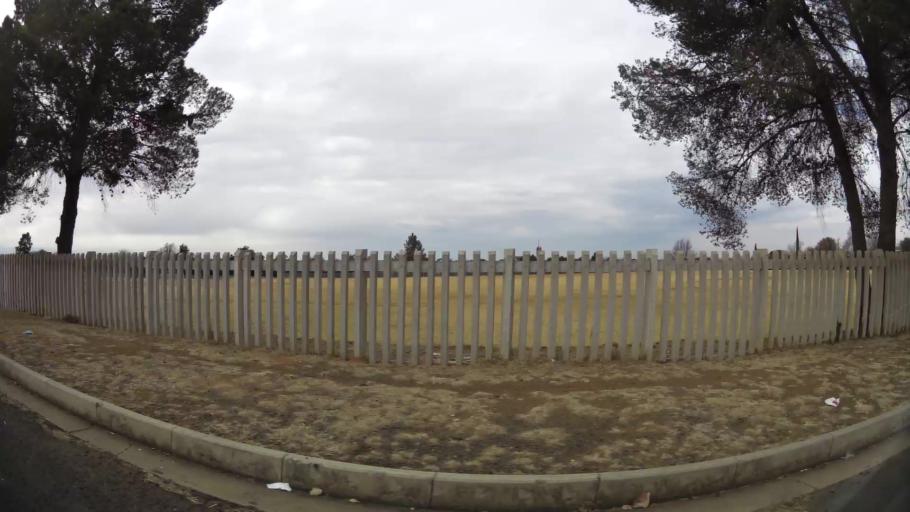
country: ZA
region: Orange Free State
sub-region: Fezile Dabi District Municipality
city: Kroonstad
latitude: -27.6398
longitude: 27.2340
